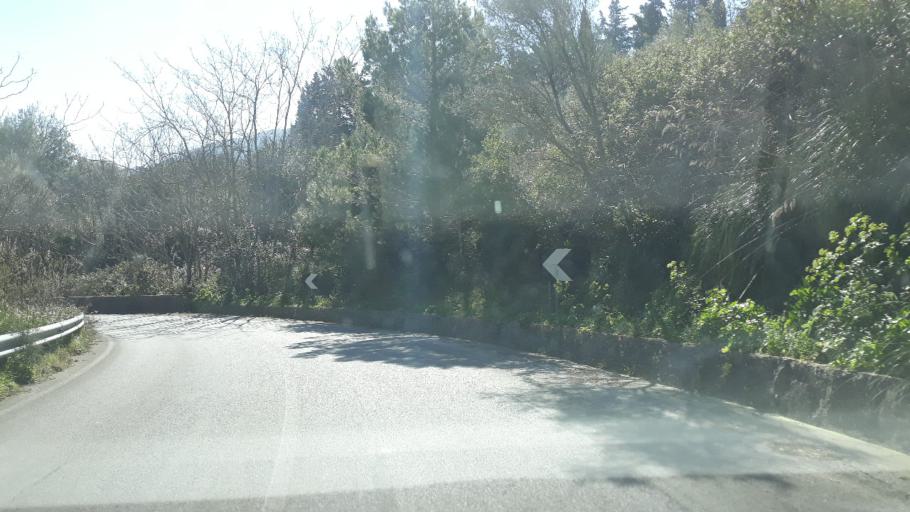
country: IT
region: Sicily
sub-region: Palermo
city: Piano dei Geli
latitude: 38.0926
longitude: 13.2574
